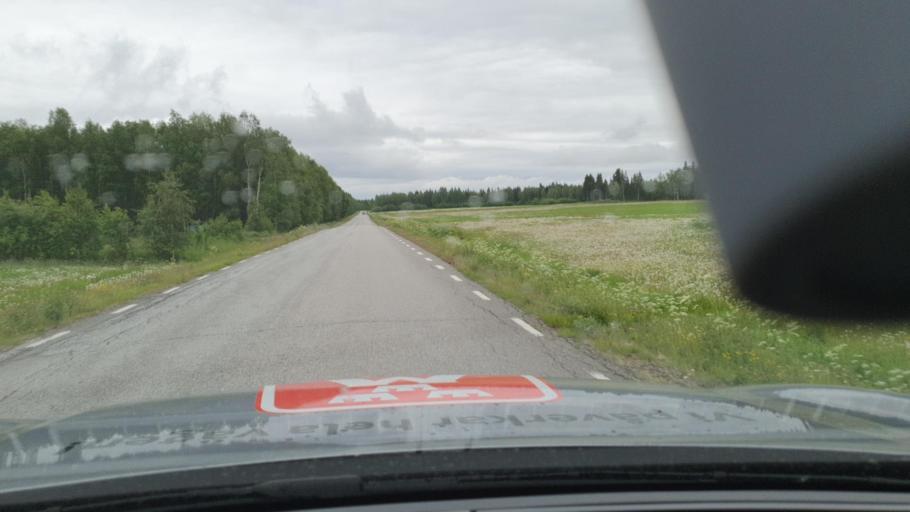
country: SE
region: Norrbotten
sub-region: Kalix Kommun
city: Toere
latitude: 65.8786
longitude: 22.6679
